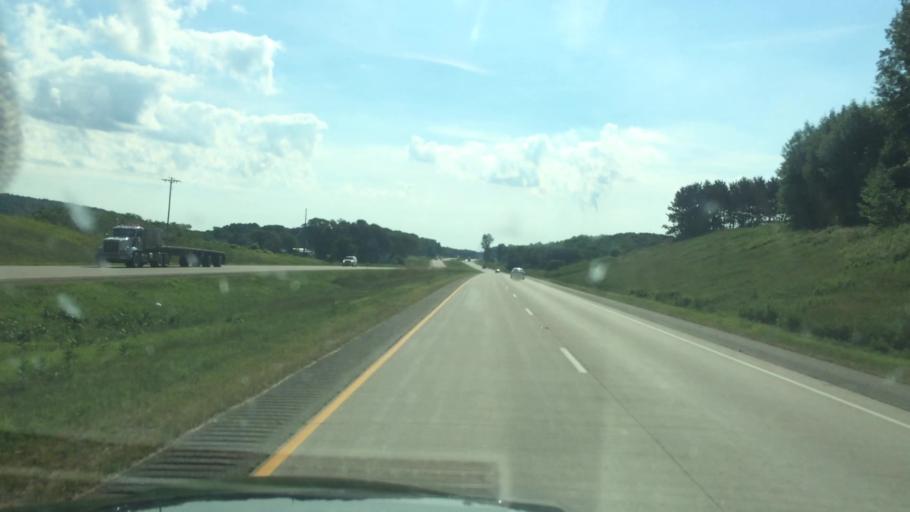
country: US
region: Wisconsin
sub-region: Shawano County
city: Wittenberg
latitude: 44.8258
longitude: -89.0936
